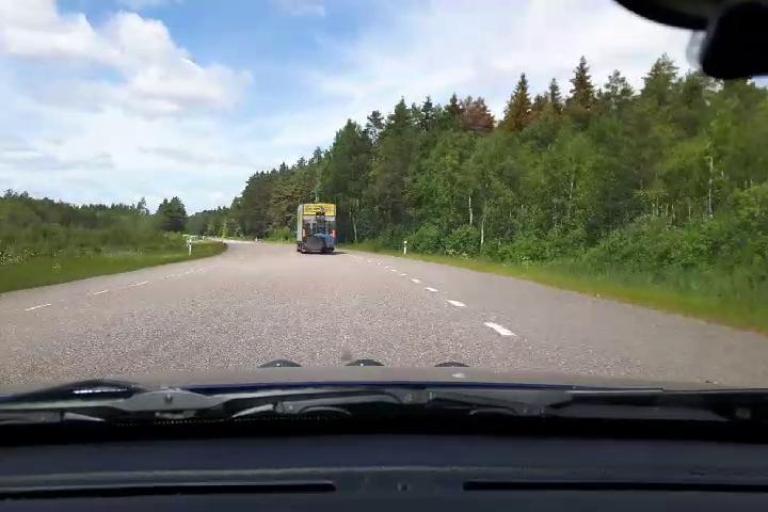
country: SE
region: Uppsala
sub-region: Osthammars Kommun
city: Bjorklinge
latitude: 60.1003
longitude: 17.5530
